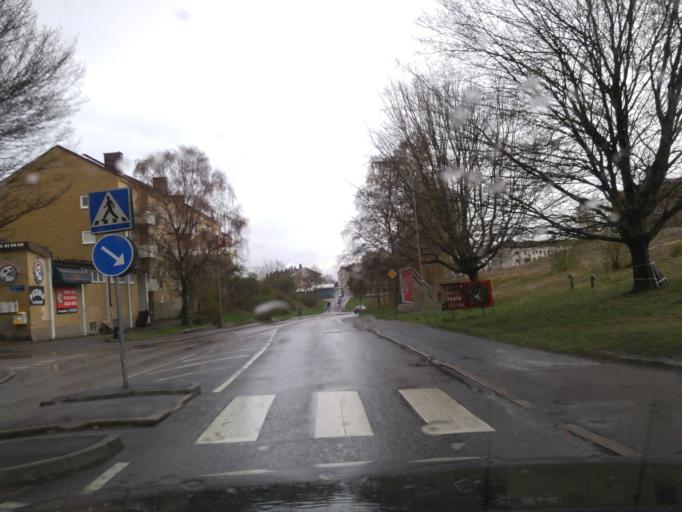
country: SE
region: Vaestra Goetaland
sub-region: Goteborg
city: Majorna
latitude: 57.6737
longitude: 11.9257
